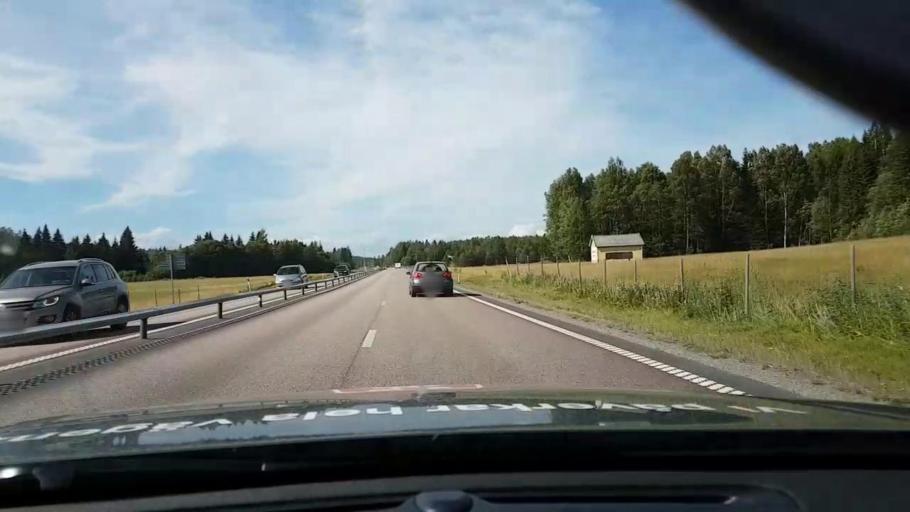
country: SE
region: Vaesternorrland
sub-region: OErnskoeldsviks Kommun
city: Ornskoldsvik
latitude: 63.2998
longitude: 18.8647
